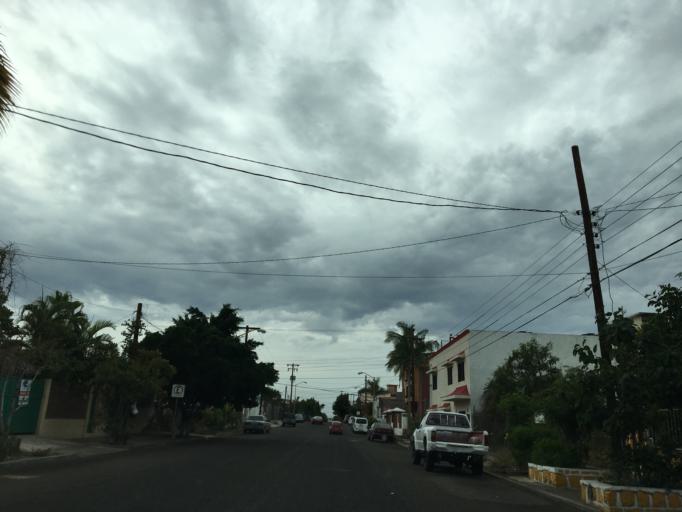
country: MX
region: Baja California Sur
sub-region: La Paz
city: La Paz
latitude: 24.1567
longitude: -110.3190
